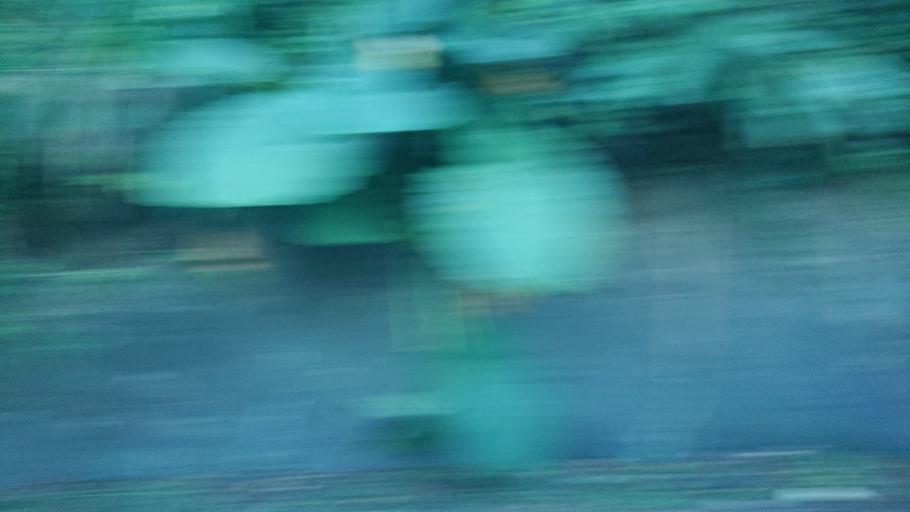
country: TW
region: Taiwan
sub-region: Chiayi
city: Jiayi Shi
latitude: 23.5174
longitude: 120.6233
